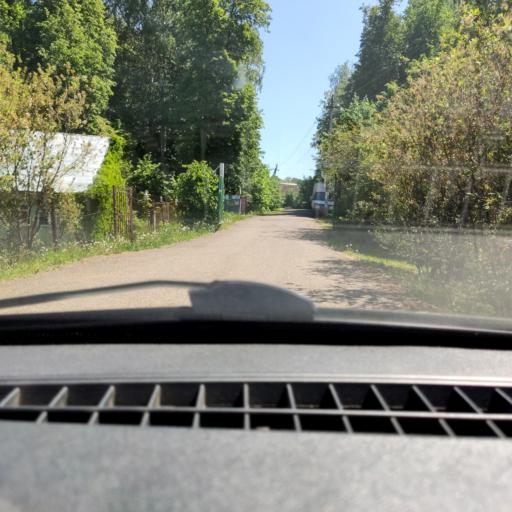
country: RU
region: Bashkortostan
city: Kabakovo
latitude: 54.4302
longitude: 55.9117
